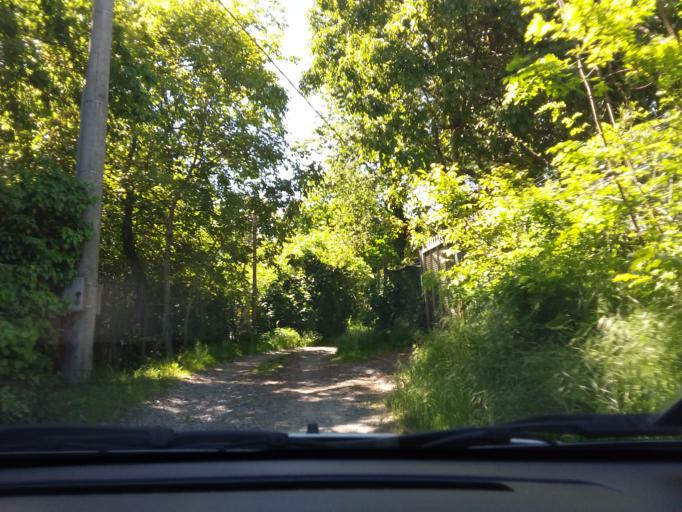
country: IT
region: Piedmont
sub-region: Provincia di Torino
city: Villarbasse
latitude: 45.0575
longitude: 7.4856
